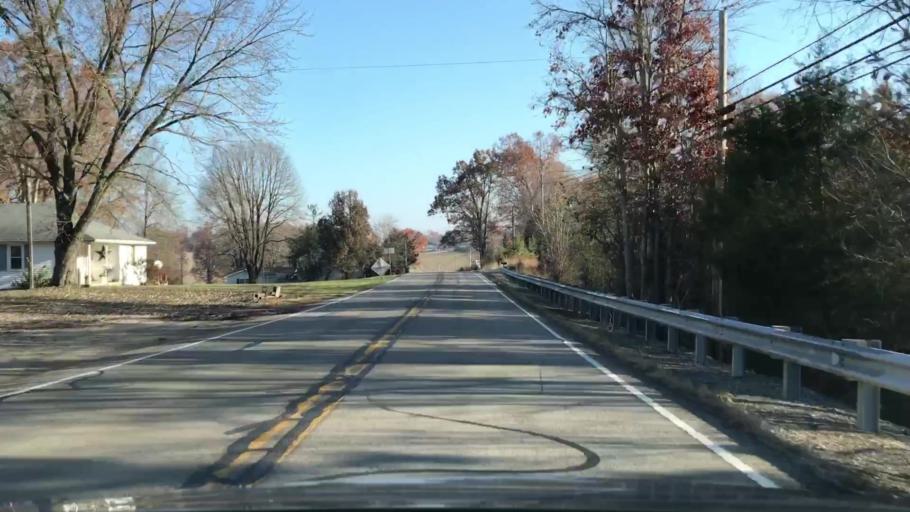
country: US
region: Kentucky
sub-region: Edmonson County
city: Brownsville
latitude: 37.2425
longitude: -86.2852
